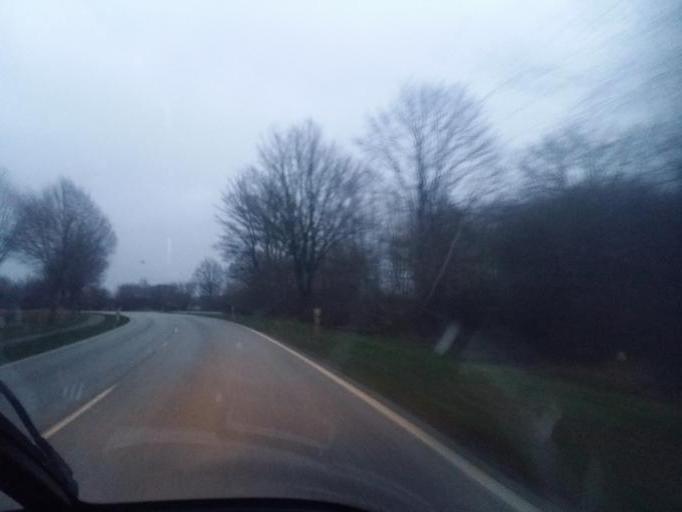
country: DE
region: Schleswig-Holstein
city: Gokels
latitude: 54.1174
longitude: 9.4497
